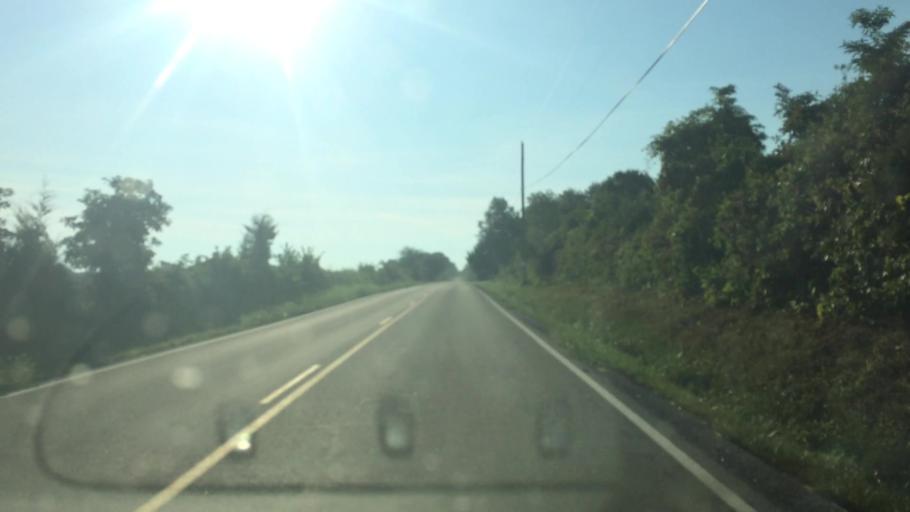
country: US
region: Missouri
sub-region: Greene County
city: Strafford
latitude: 37.2559
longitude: -93.1845
